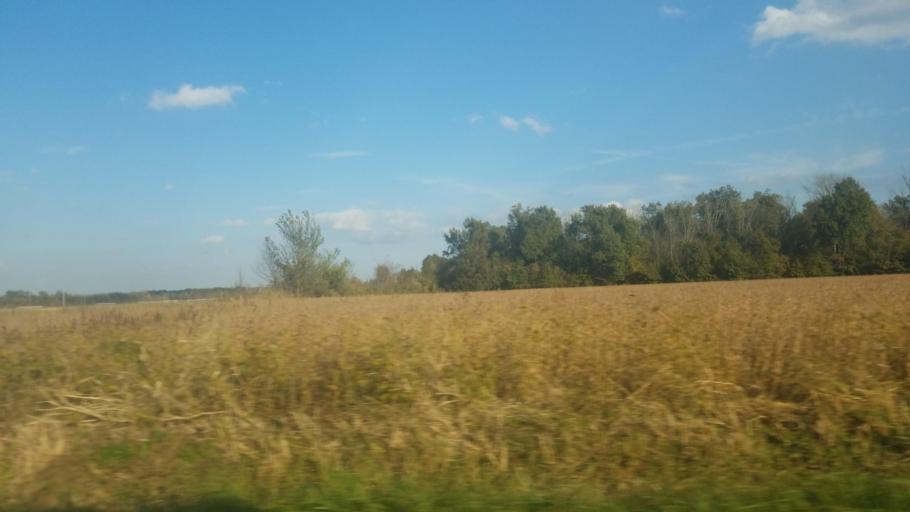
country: US
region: Illinois
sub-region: Saline County
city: Harrisburg
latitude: 37.8229
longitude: -88.6147
